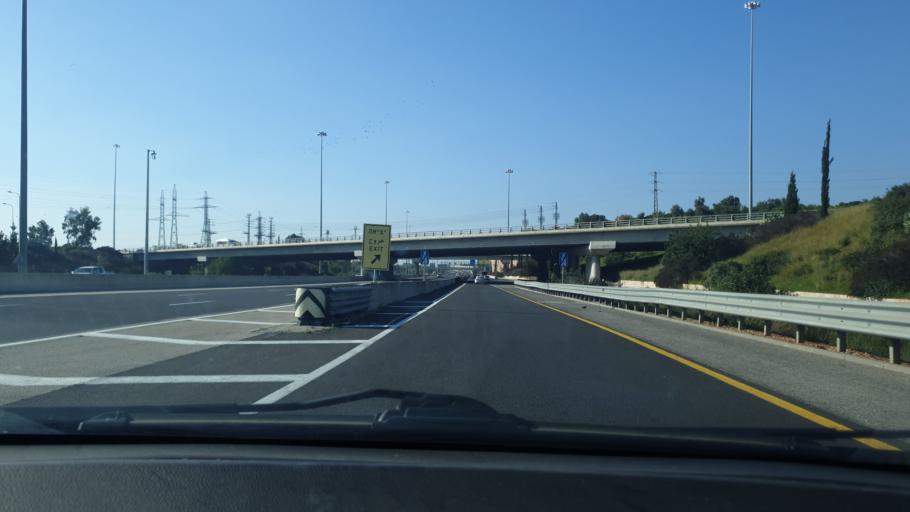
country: IL
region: Central District
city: Rishon LeZiyyon
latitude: 31.9574
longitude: 34.7765
